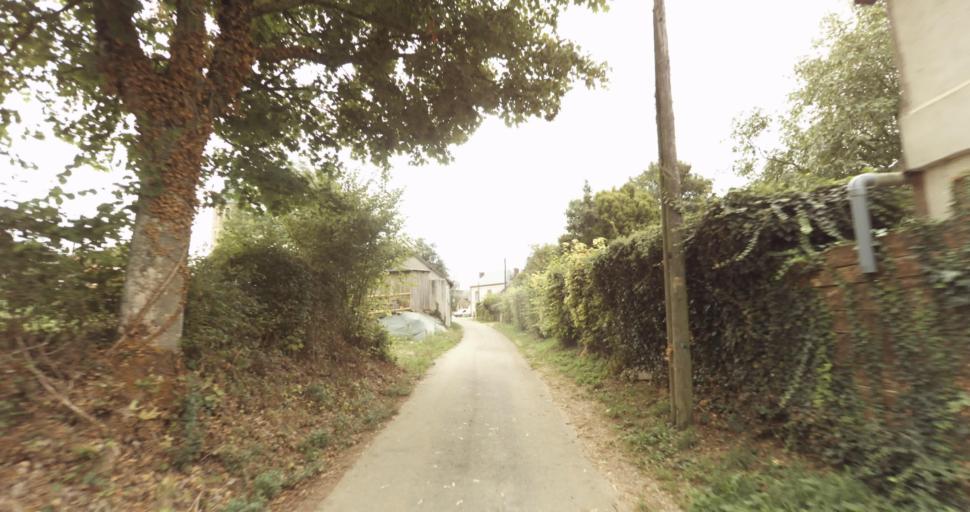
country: FR
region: Lower Normandy
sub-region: Departement de l'Orne
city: Gace
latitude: 48.7631
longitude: 0.3404
